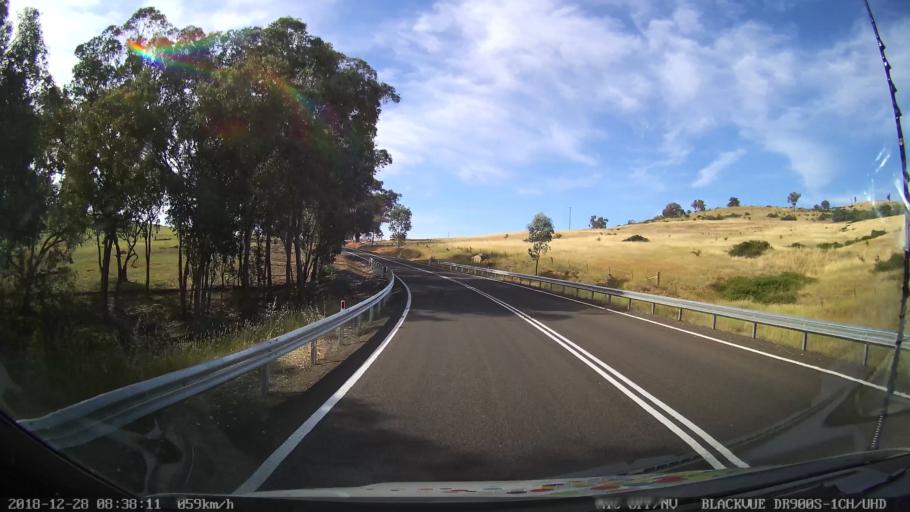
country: AU
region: New South Wales
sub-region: Blayney
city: Blayney
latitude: -34.0014
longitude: 149.3146
